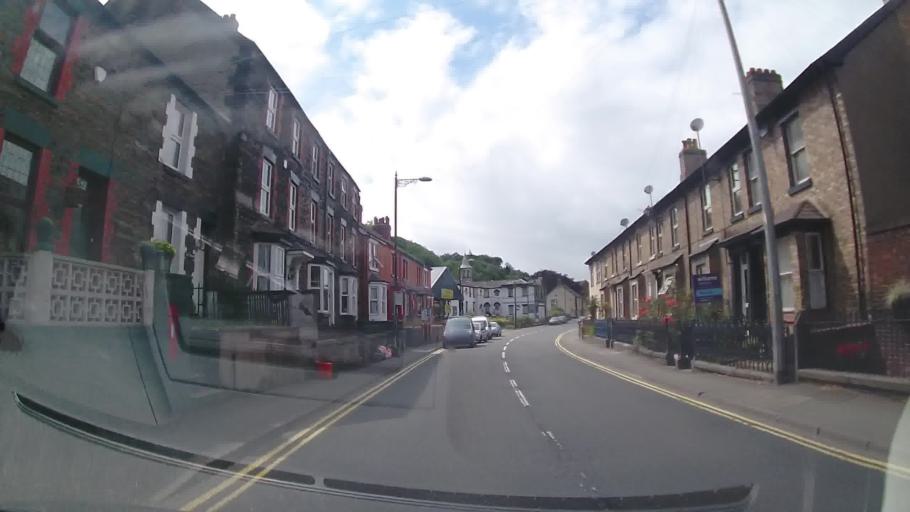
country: GB
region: Wales
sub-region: Denbighshire
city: Corwen
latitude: 52.9787
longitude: -3.3686
